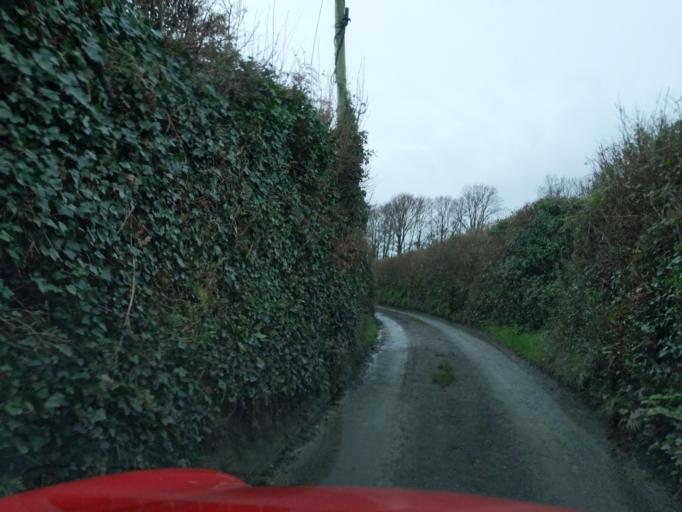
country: GB
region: England
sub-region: Cornwall
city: Fowey
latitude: 50.3378
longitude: -4.5829
